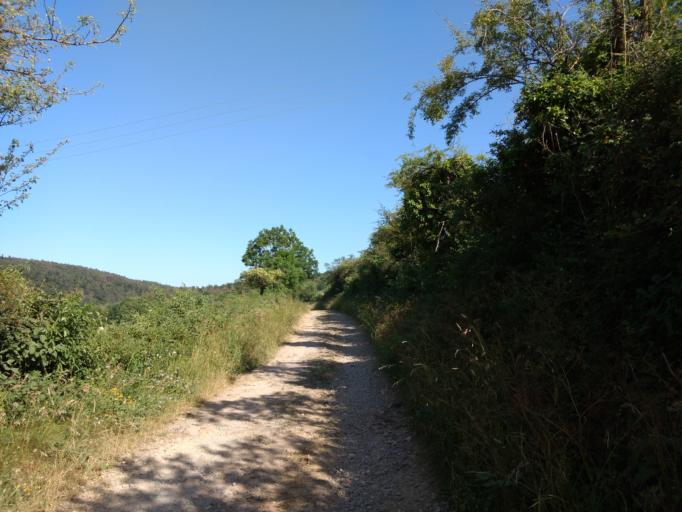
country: FR
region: Midi-Pyrenees
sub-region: Departement de l'Aveyron
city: La Loubiere
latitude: 44.3623
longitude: 2.6859
